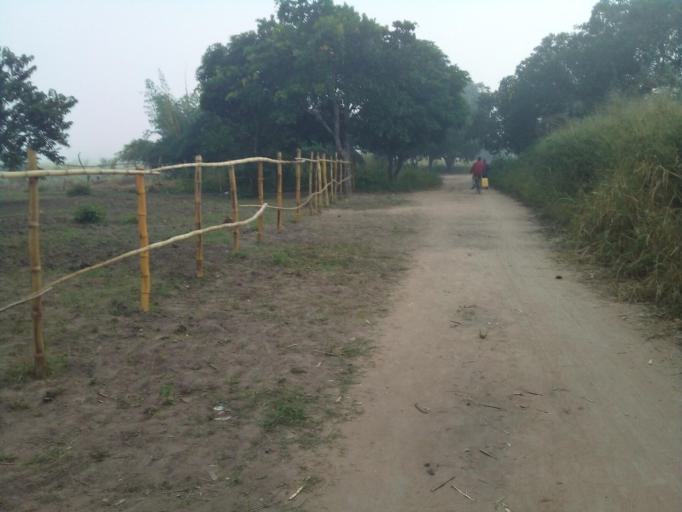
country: MZ
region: Zambezia
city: Quelimane
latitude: -17.5917
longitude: 36.6849
